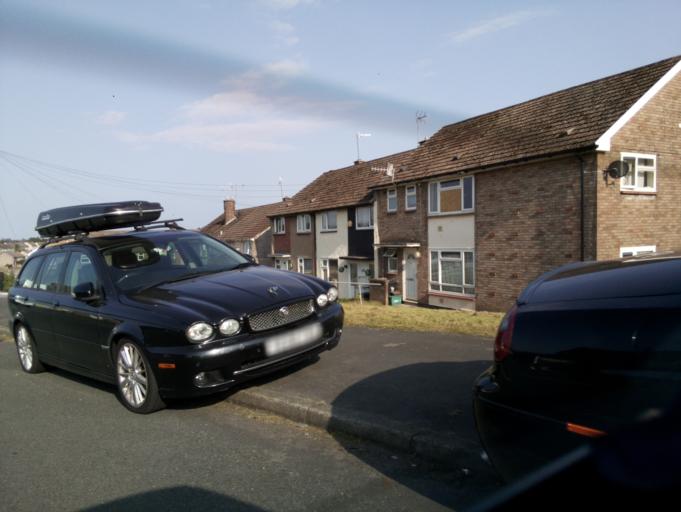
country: GB
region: Wales
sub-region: Newport
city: Newport
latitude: 51.6108
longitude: -3.0345
